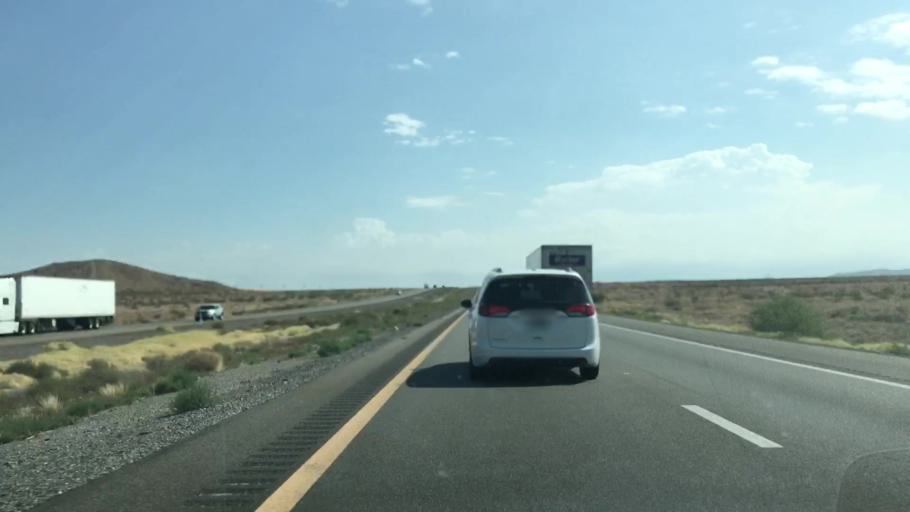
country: US
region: Nevada
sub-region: Clark County
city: Moapa Town
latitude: 36.4722
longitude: -114.8199
